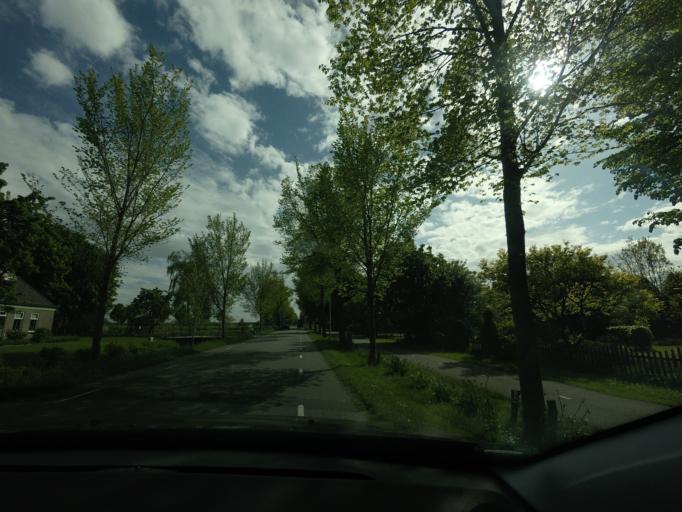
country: NL
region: North Holland
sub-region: Gemeente Beemster
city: Halfweg
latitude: 52.5649
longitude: 4.9229
